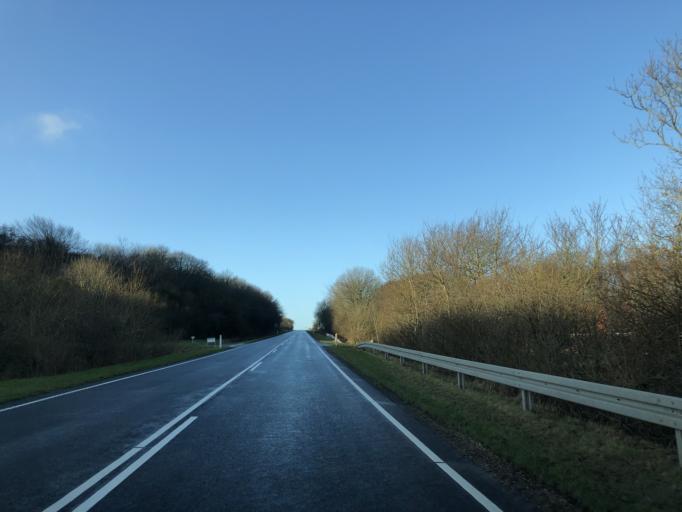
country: DK
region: Central Jutland
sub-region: Lemvig Kommune
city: Lemvig
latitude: 56.5583
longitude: 8.4347
